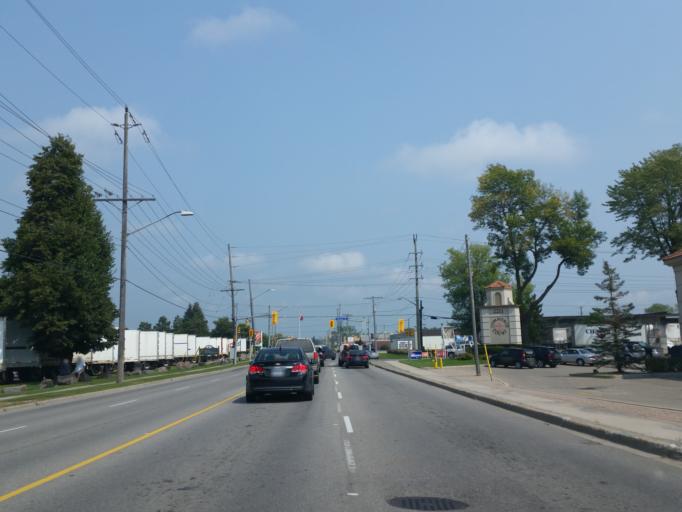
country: CA
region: Ontario
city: Brockville
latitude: 44.6084
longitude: -75.6934
